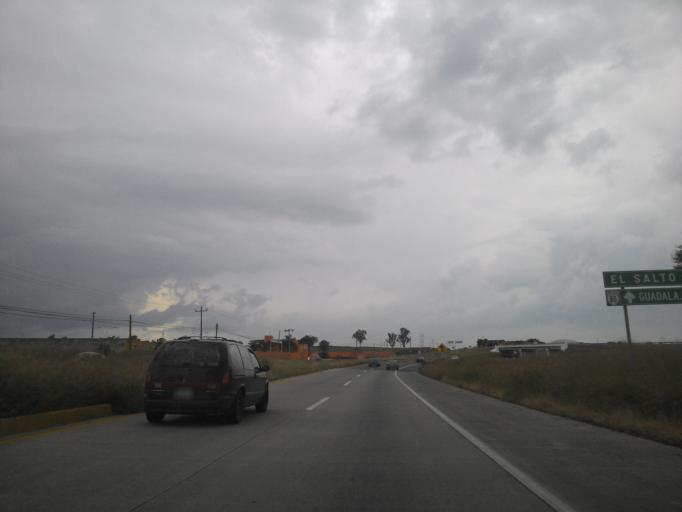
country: MX
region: Jalisco
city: Puente Grande
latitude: 20.5751
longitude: -103.1314
